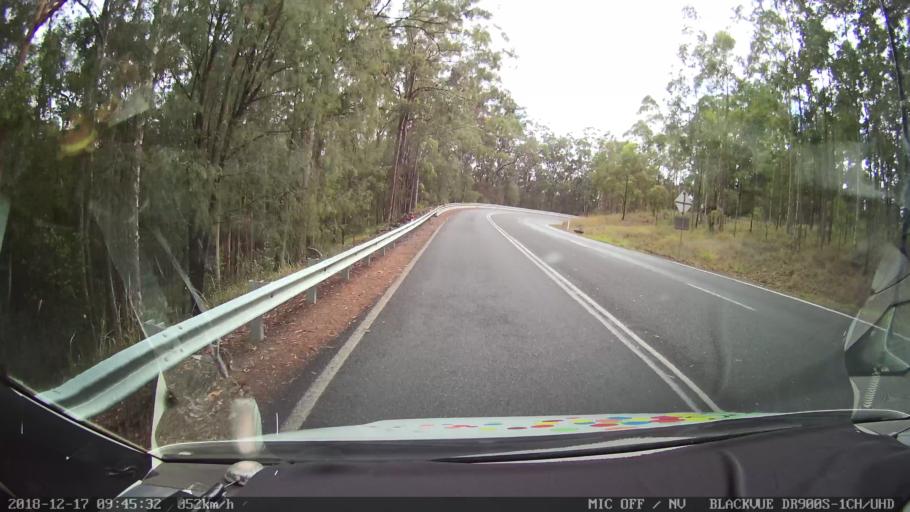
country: AU
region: New South Wales
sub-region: Tenterfield Municipality
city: Carrolls Creek
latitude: -28.9254
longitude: 152.3304
